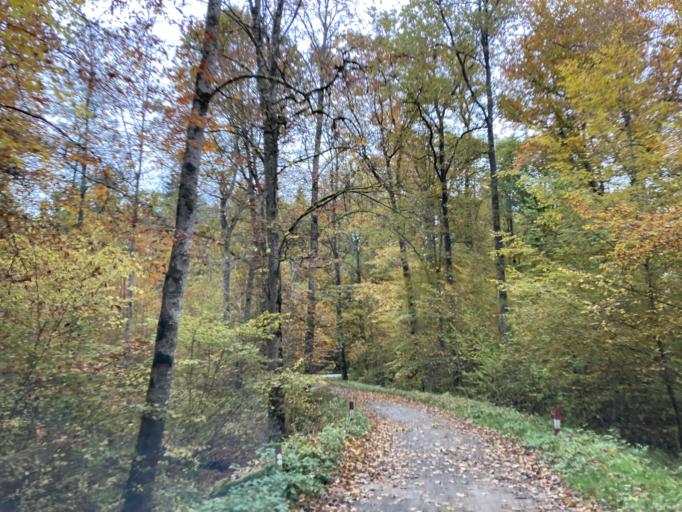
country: DE
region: Baden-Wuerttemberg
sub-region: Tuebingen Region
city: Ofterdingen
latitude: 48.4623
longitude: 8.9986
